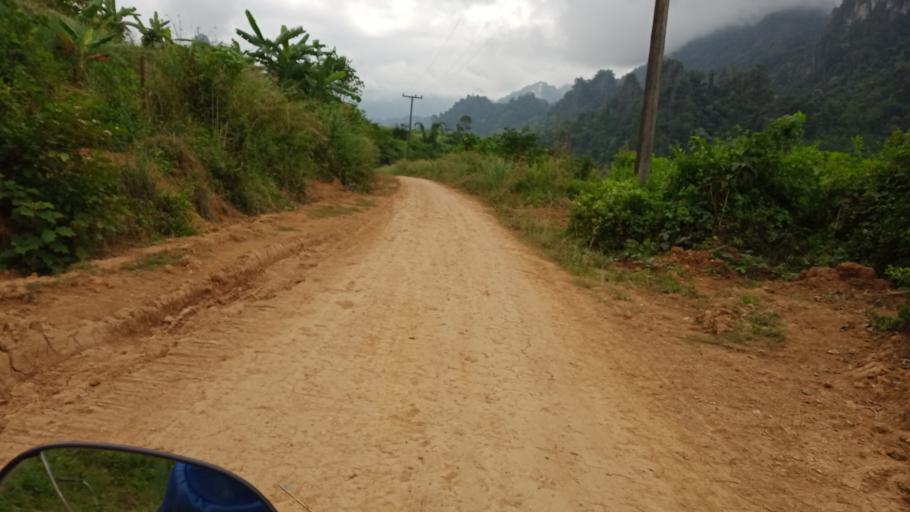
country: LA
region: Xiangkhoang
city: Phonsavan
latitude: 19.0916
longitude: 103.0053
